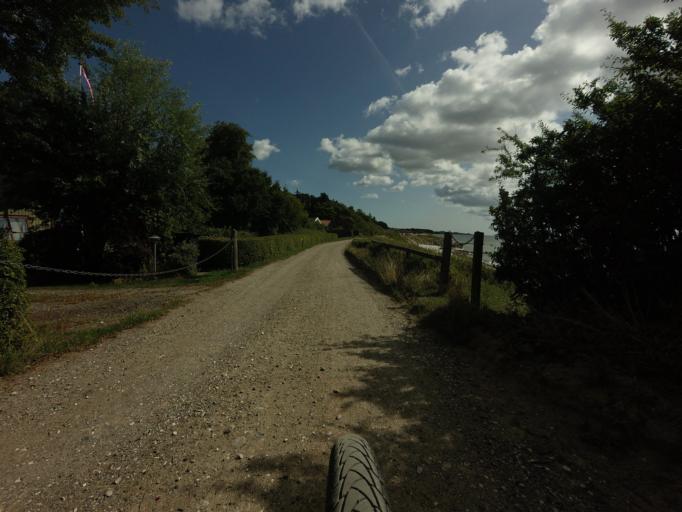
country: DK
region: Zealand
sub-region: Vordingborg Kommune
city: Stege
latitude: 54.9627
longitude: 12.4165
